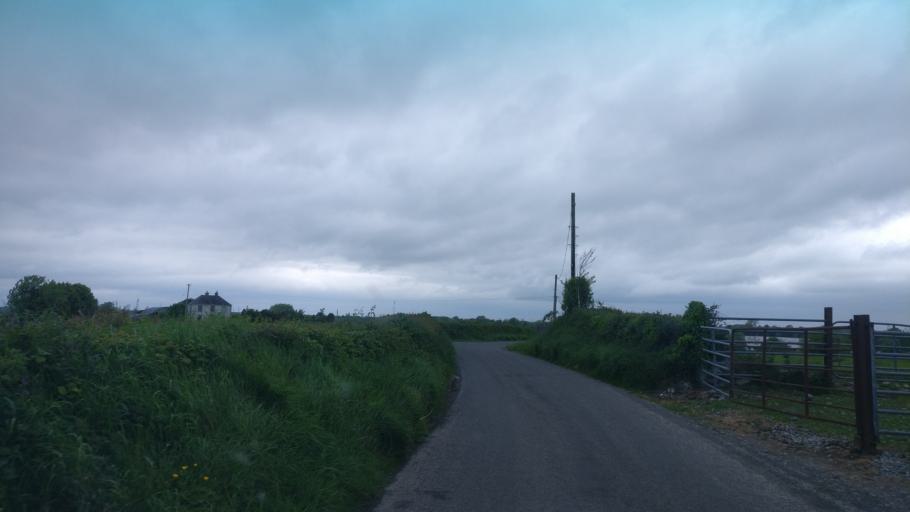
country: IE
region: Connaught
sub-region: County Galway
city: Portumna
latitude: 53.1309
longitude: -8.2898
